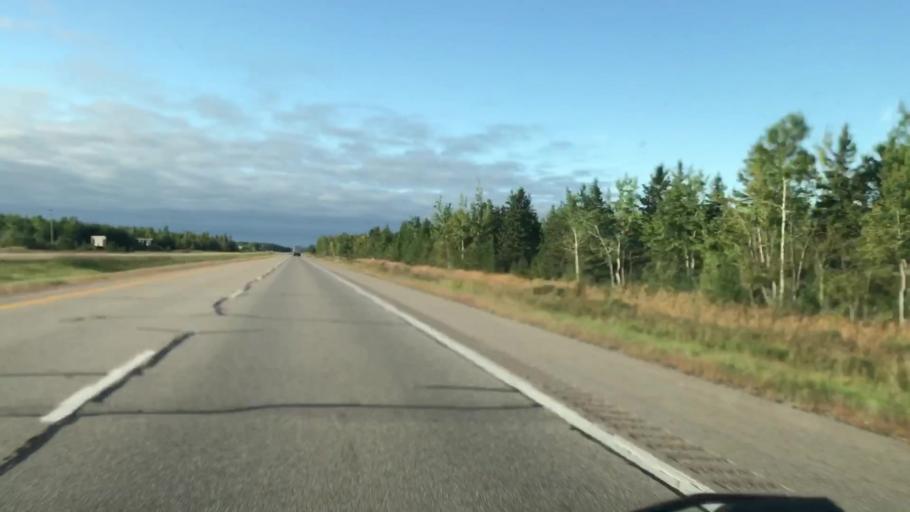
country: US
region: Michigan
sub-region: Chippewa County
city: Sault Ste. Marie
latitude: 46.4079
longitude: -84.3999
